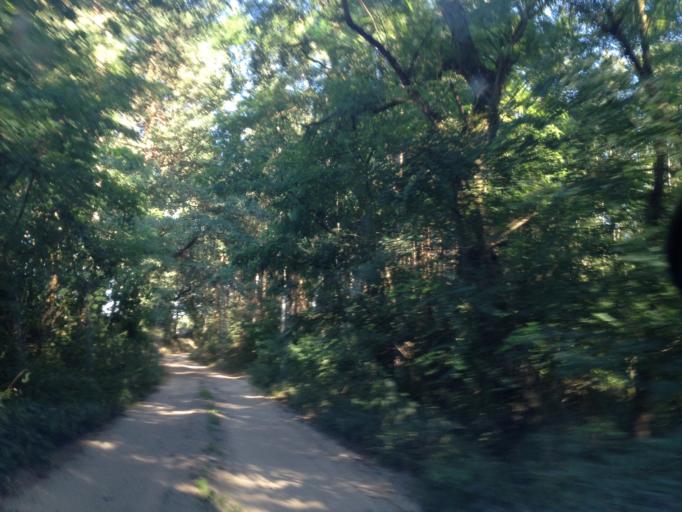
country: PL
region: Greater Poland Voivodeship
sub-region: Powiat sredzki
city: Zaniemysl
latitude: 52.1065
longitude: 17.1285
